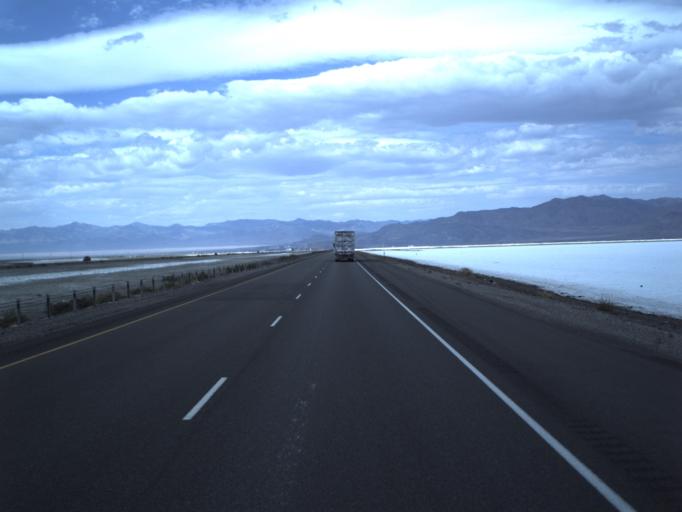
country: US
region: Utah
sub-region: Tooele County
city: Wendover
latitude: 40.7403
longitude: -113.8973
